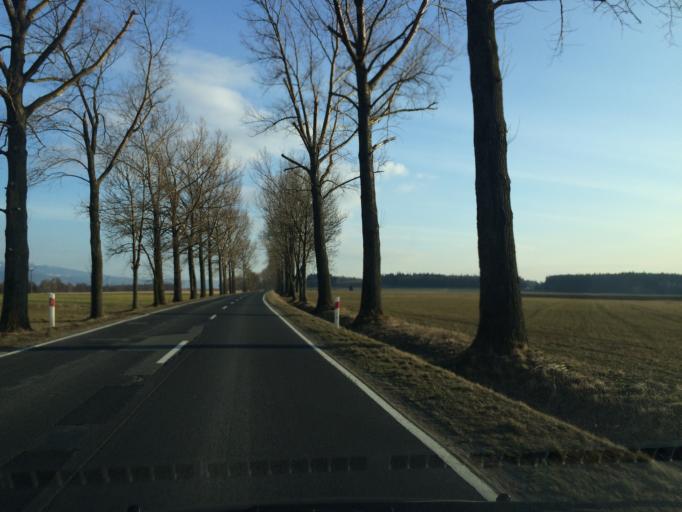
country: PL
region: Lower Silesian Voivodeship
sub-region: Powiat klodzki
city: Bystrzyca Klodzka
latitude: 50.2525
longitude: 16.6657
